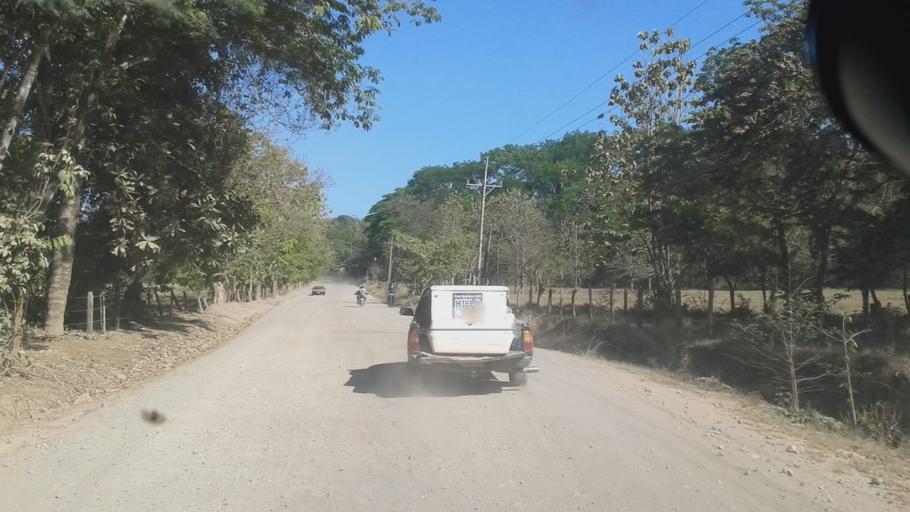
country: CR
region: Guanacaste
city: Samara
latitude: 9.9119
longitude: -85.6190
